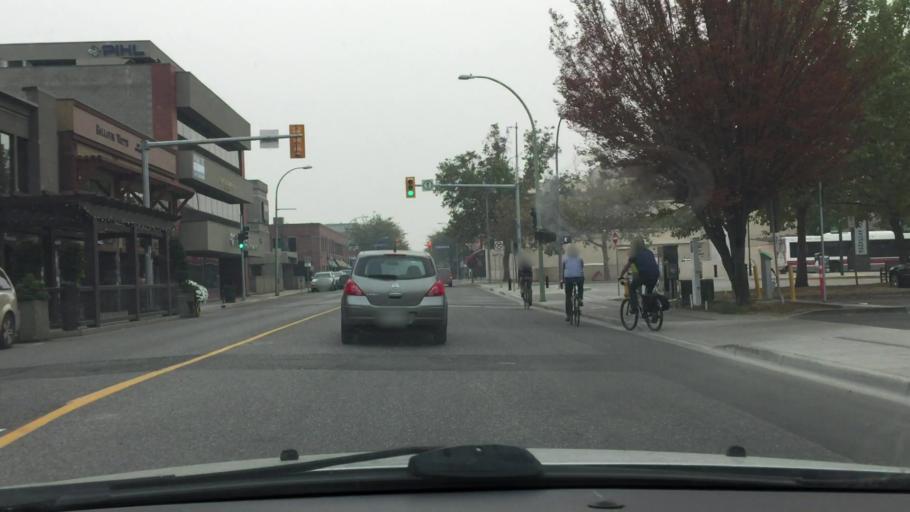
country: CA
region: British Columbia
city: Kelowna
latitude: 49.8878
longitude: -119.4936
